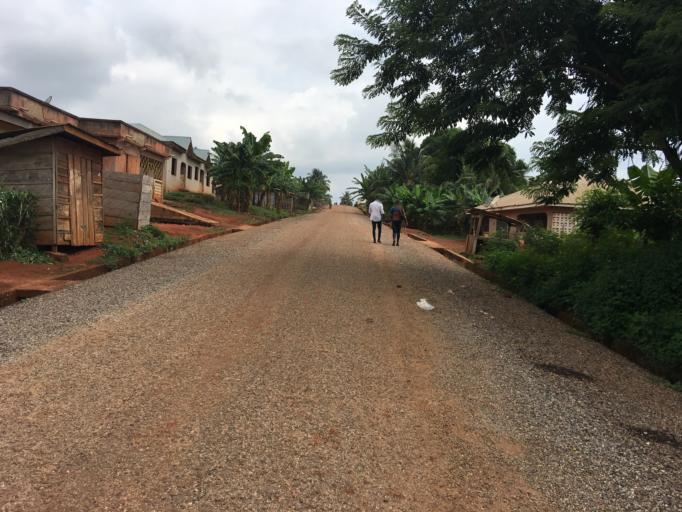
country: GH
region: Western
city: Bibiani
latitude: 6.8099
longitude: -2.5233
